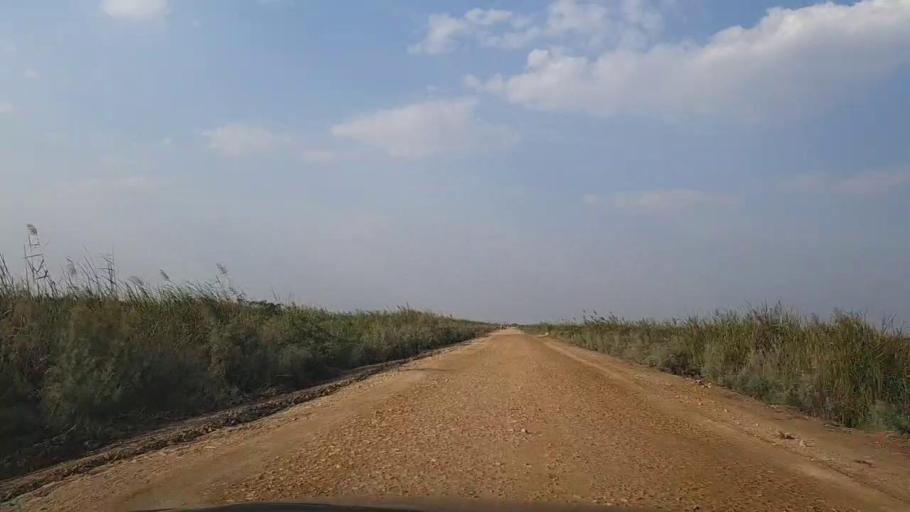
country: PK
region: Sindh
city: Gharo
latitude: 24.7776
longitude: 67.7466
